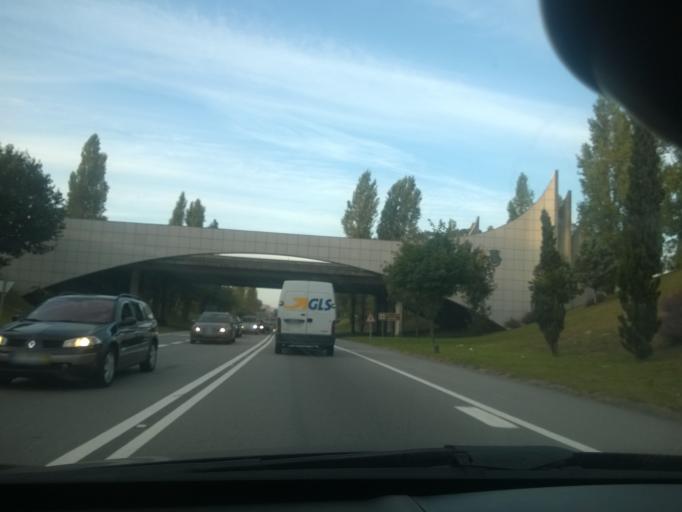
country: PT
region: Porto
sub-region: Maia
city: Maia
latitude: 41.2268
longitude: -8.6263
